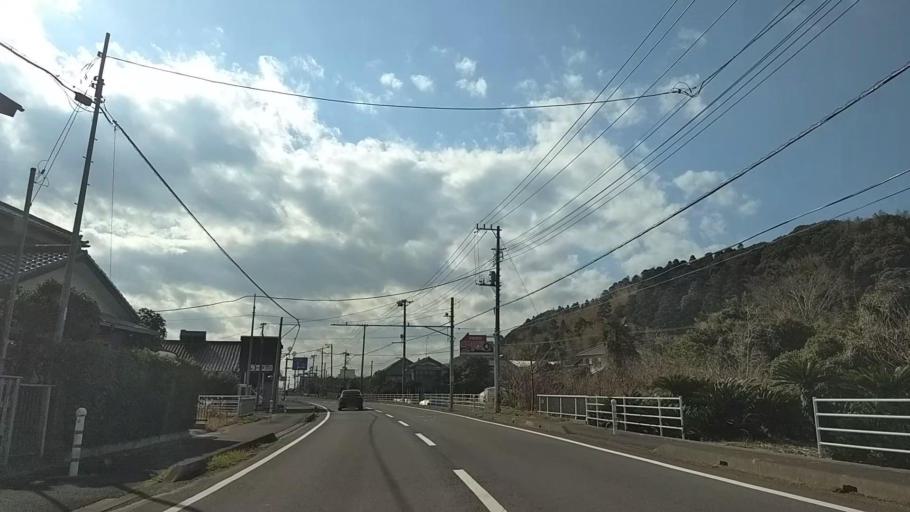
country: JP
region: Chiba
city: Naruto
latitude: 35.6238
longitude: 140.4403
